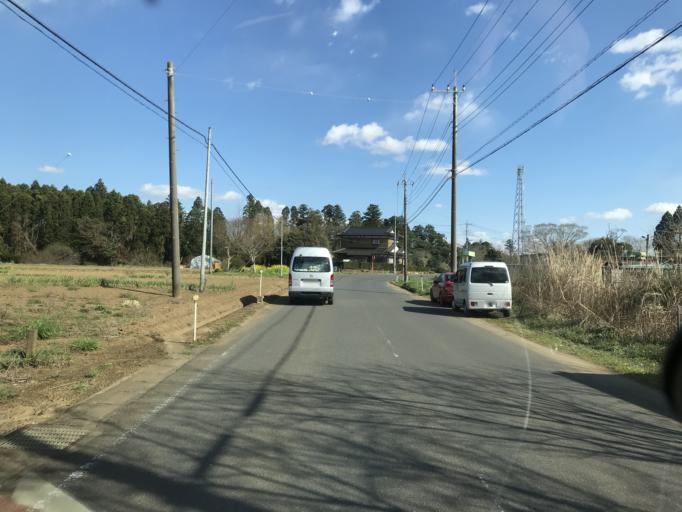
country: JP
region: Chiba
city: Sawara
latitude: 35.8555
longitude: 140.4172
